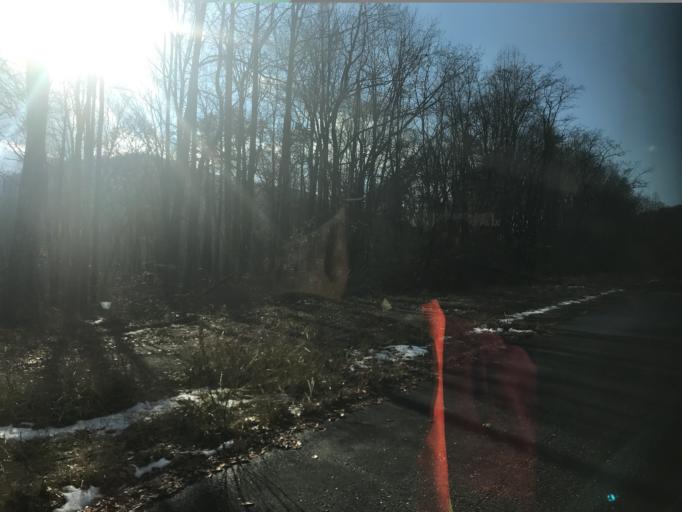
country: US
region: Pennsylvania
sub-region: Fulton County
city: McConnellsburg
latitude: 40.0495
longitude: -78.1020
